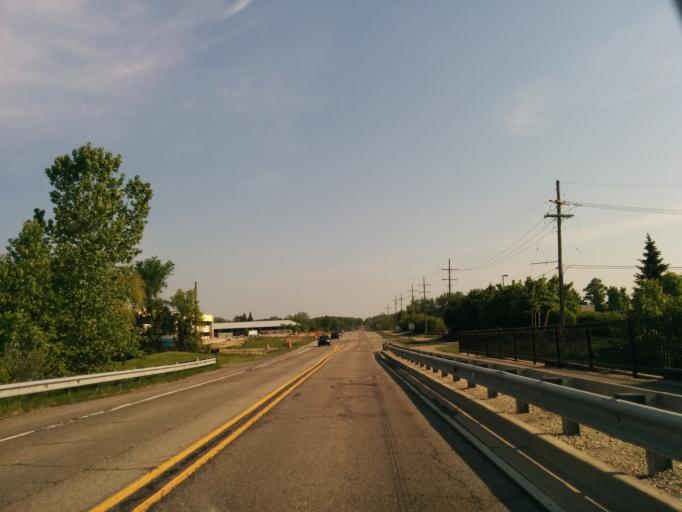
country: US
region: Michigan
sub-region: Oakland County
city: Novi
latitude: 42.4871
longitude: -83.4561
